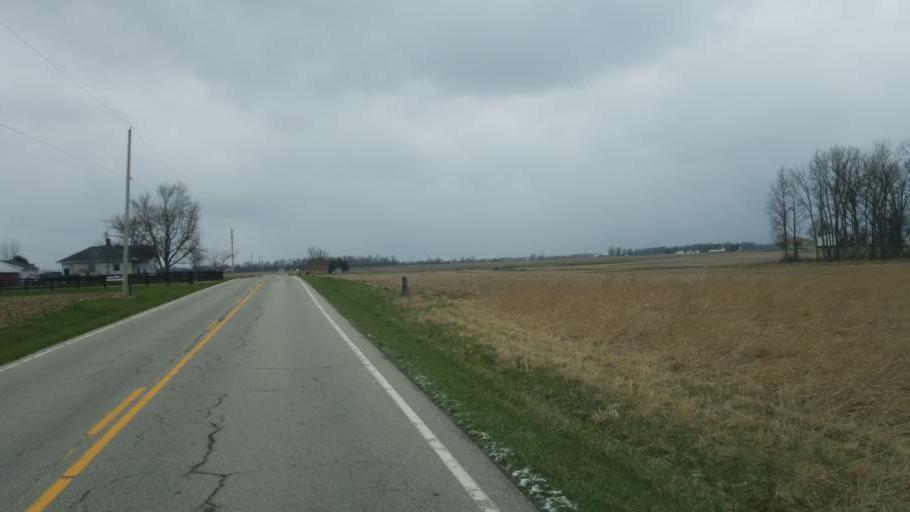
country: US
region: Ohio
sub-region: Union County
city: Richwood
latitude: 40.4371
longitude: -83.3906
